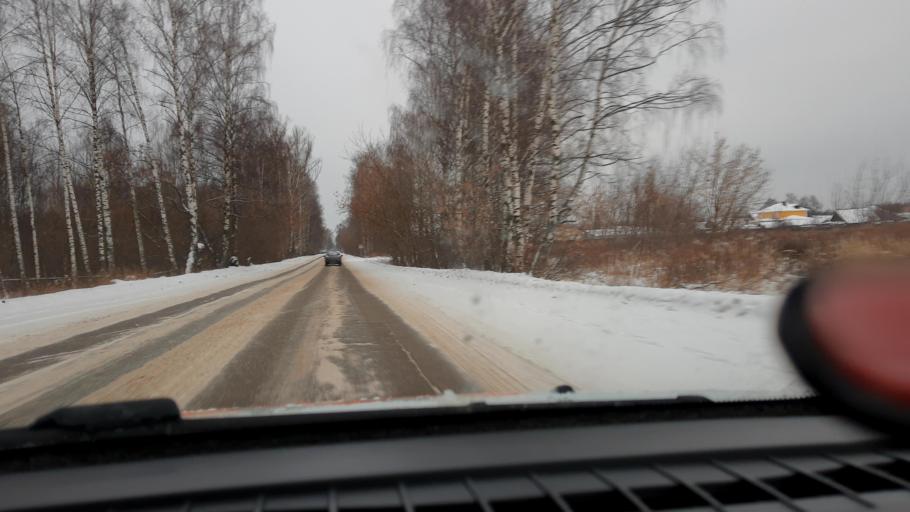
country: RU
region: Nizjnij Novgorod
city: Pamyat' Parizhskoy Kommuny
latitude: 56.2709
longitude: 44.4162
